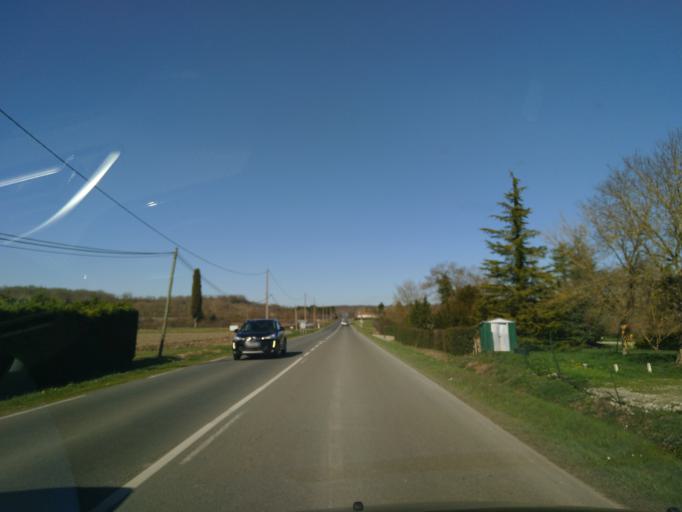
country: FR
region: Aquitaine
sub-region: Departement du Lot-et-Garonne
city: Castillonnes
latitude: 44.7078
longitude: 0.5614
